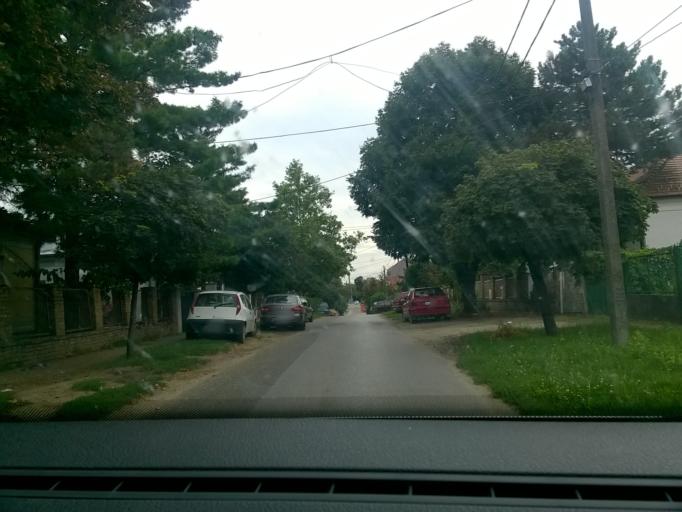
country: RS
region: Autonomna Pokrajina Vojvodina
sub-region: Juznobanatski Okrug
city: Pancevo
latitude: 44.8720
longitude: 20.6577
